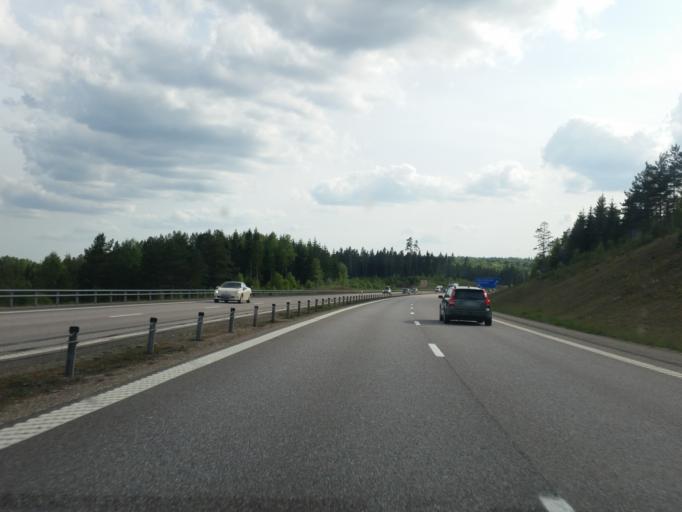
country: SE
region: Vaestra Goetaland
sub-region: Boras Kommun
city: Dalsjofors
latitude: 57.7639
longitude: 13.1104
